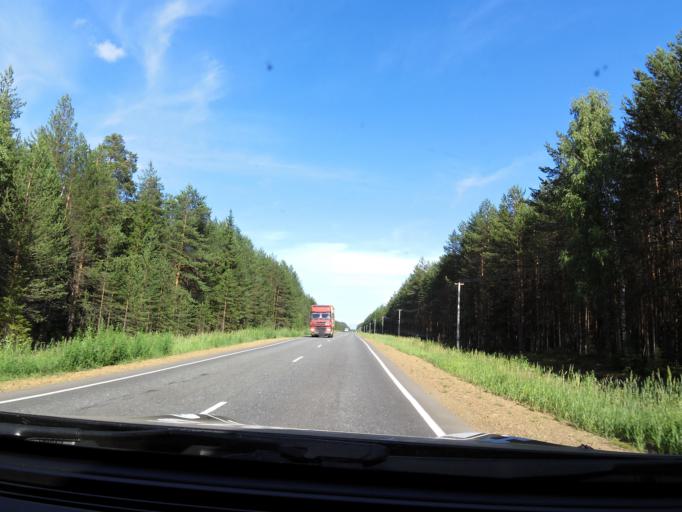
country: RU
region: Kirov
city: Belaya Kholunitsa
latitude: 58.9081
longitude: 50.9956
